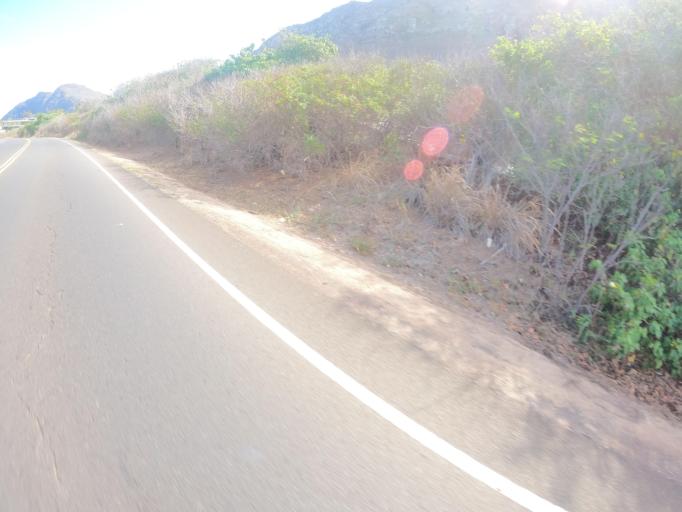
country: US
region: Hawaii
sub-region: Honolulu County
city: Waimanalo Beach
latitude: 21.3166
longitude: -157.6673
